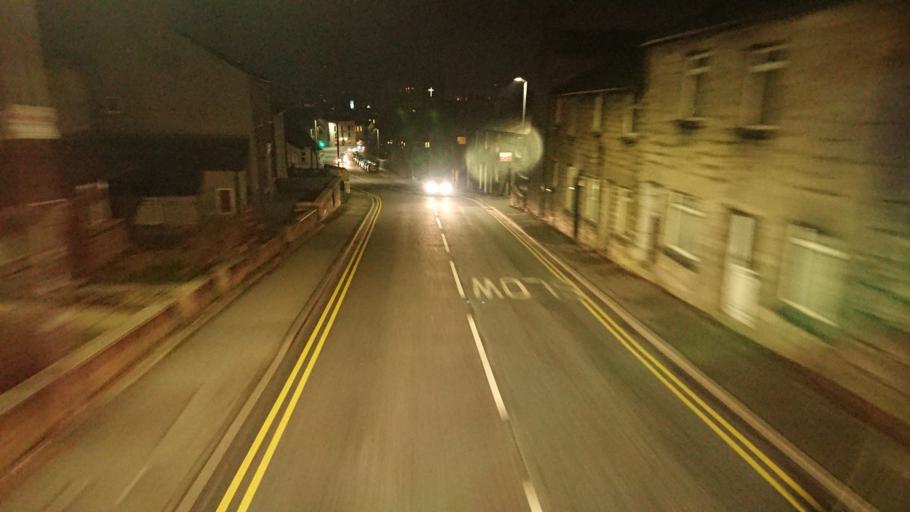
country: GB
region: England
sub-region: Cumbria
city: Kendal
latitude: 54.3326
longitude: -2.7522
